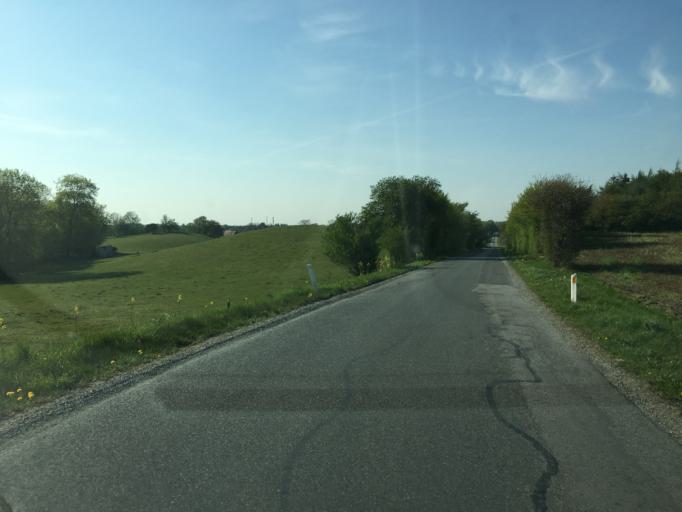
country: DK
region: South Denmark
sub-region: Haderslev Kommune
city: Vojens
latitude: 55.2336
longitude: 9.3299
